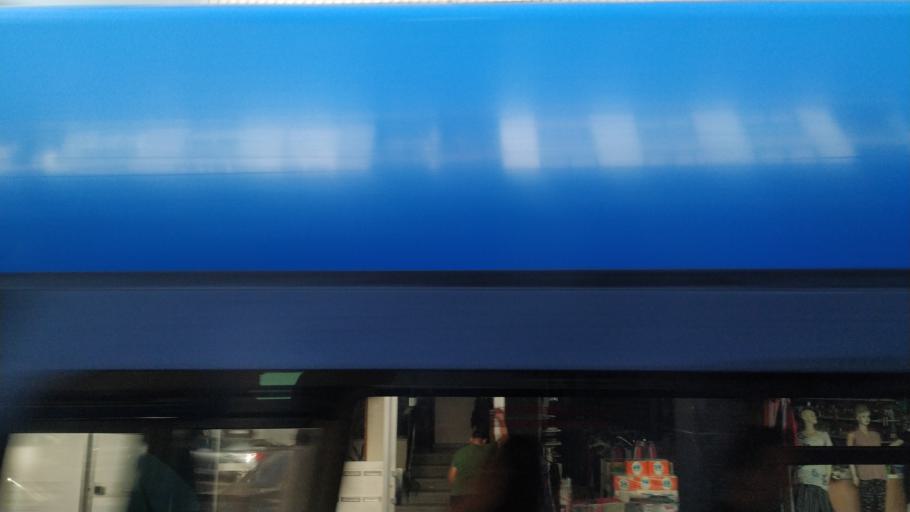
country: PT
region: Porto
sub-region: Vila Nova de Gaia
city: Vilar de Andorinho
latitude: 41.1189
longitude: -8.6088
